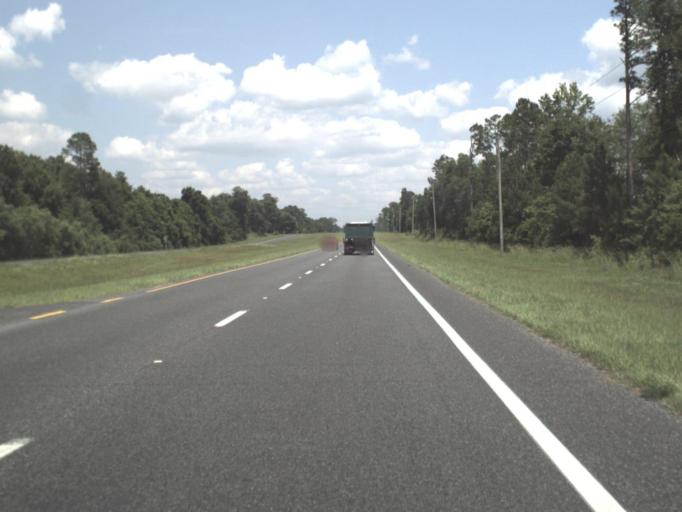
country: US
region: Florida
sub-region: Alachua County
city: Hawthorne
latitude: 29.5999
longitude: -82.1387
